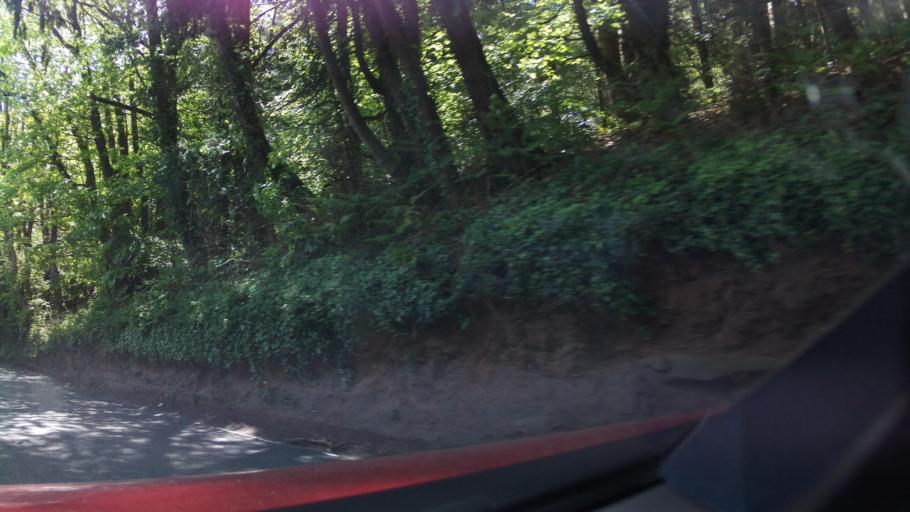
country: GB
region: England
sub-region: Devon
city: Newton Poppleford
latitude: 50.6925
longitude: -3.3054
